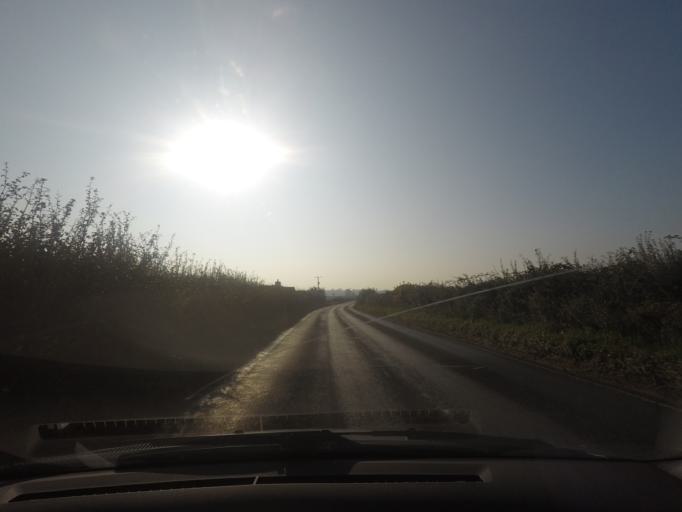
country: GB
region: England
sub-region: City and Borough of Leeds
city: Walton
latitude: 54.0196
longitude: -1.3126
